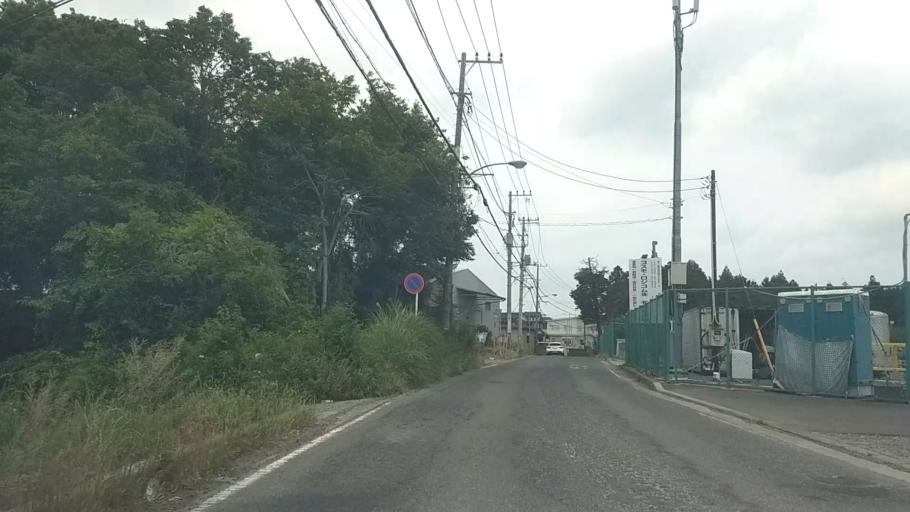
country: JP
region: Kanagawa
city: Fujisawa
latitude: 35.3619
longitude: 139.4350
